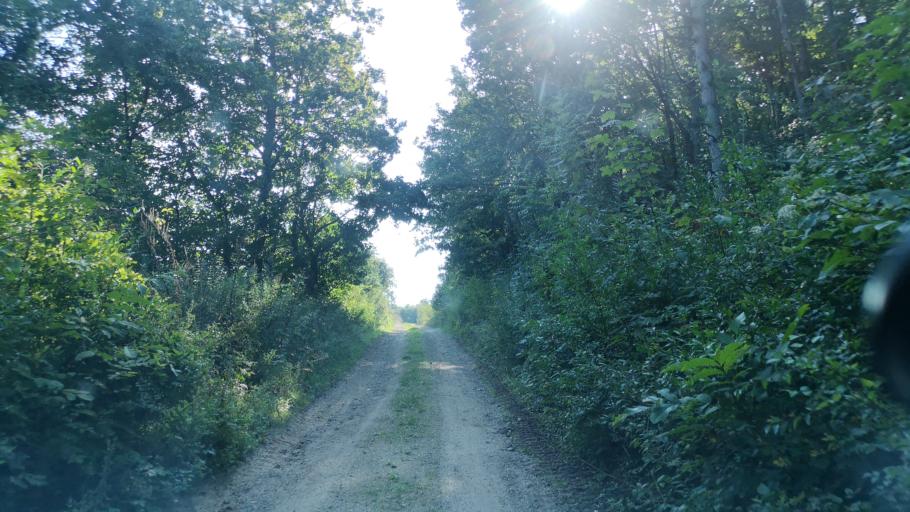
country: SK
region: Trnavsky
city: Smolenice
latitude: 48.5410
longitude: 17.4427
